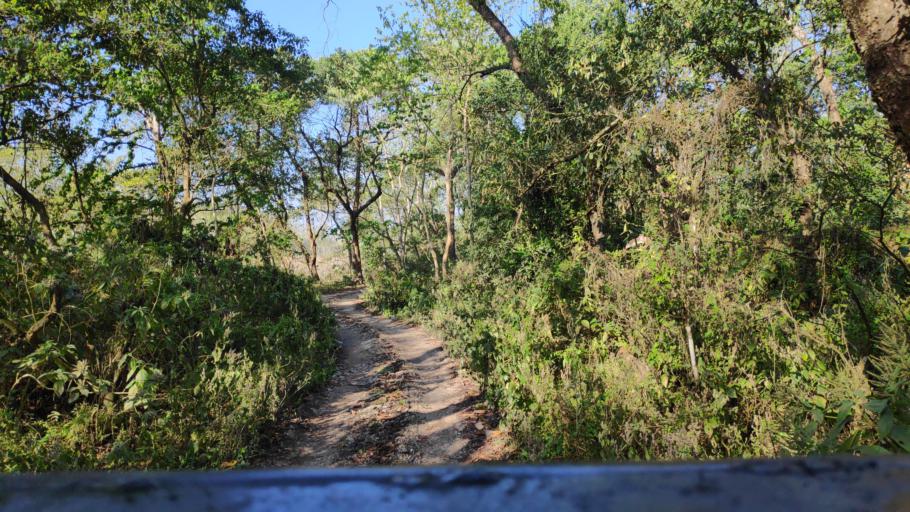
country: NP
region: Central Region
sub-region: Narayani Zone
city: Bharatpur
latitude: 27.5601
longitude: 84.5388
